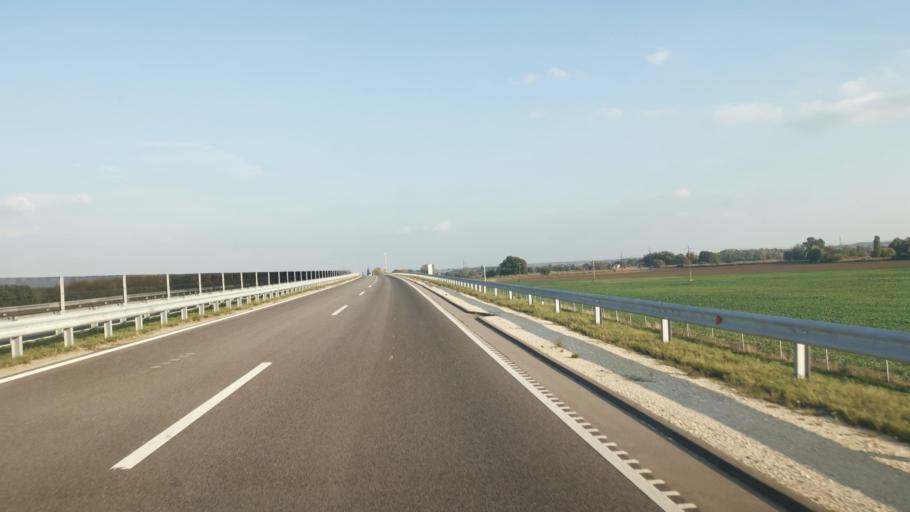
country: HU
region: Gyor-Moson-Sopron
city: Fertoszentmiklos
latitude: 47.5717
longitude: 16.7911
